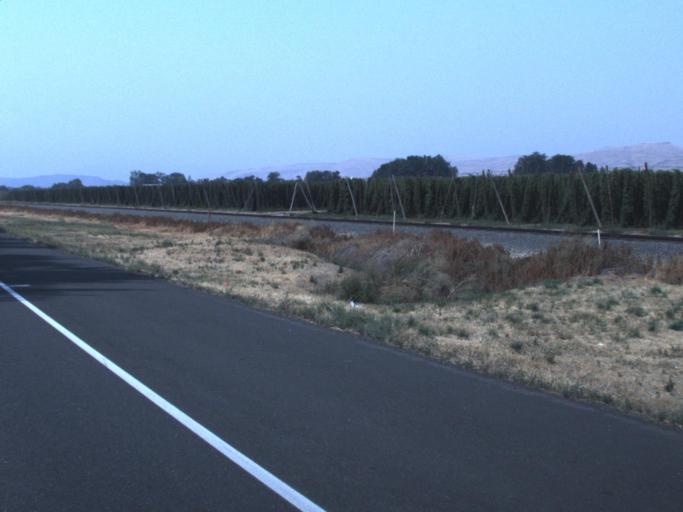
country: US
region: Washington
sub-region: Yakima County
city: Terrace Heights
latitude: 46.5705
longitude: -120.4250
